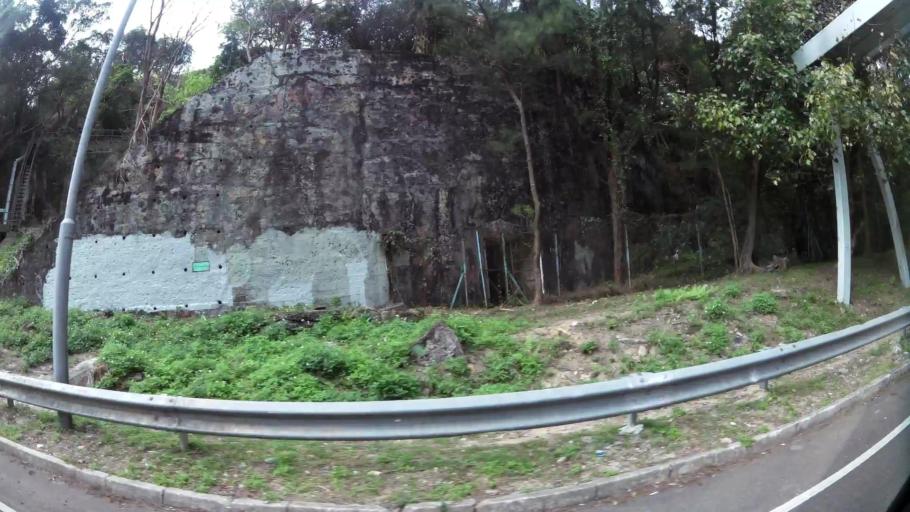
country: HK
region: Wanchai
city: Wan Chai
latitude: 22.2814
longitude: 114.2347
